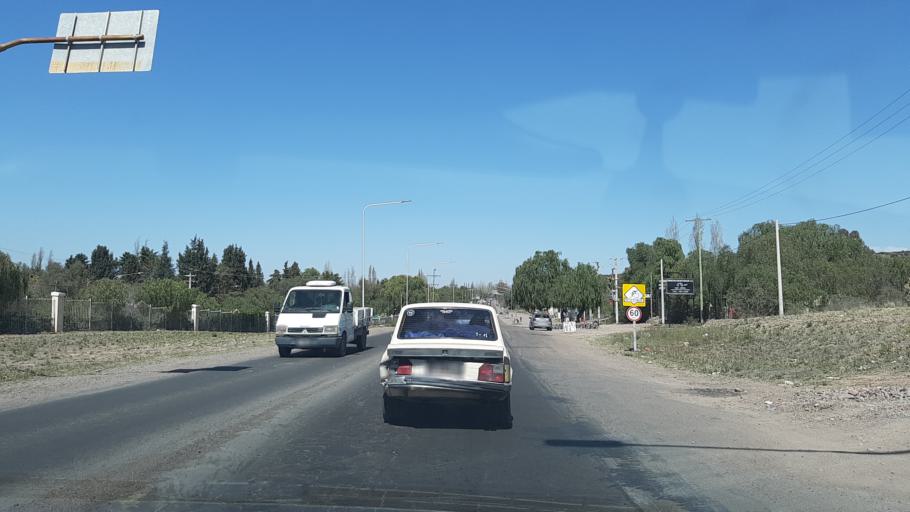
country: AR
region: Mendoza
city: Lujan de Cuyo
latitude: -32.9723
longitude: -68.8819
